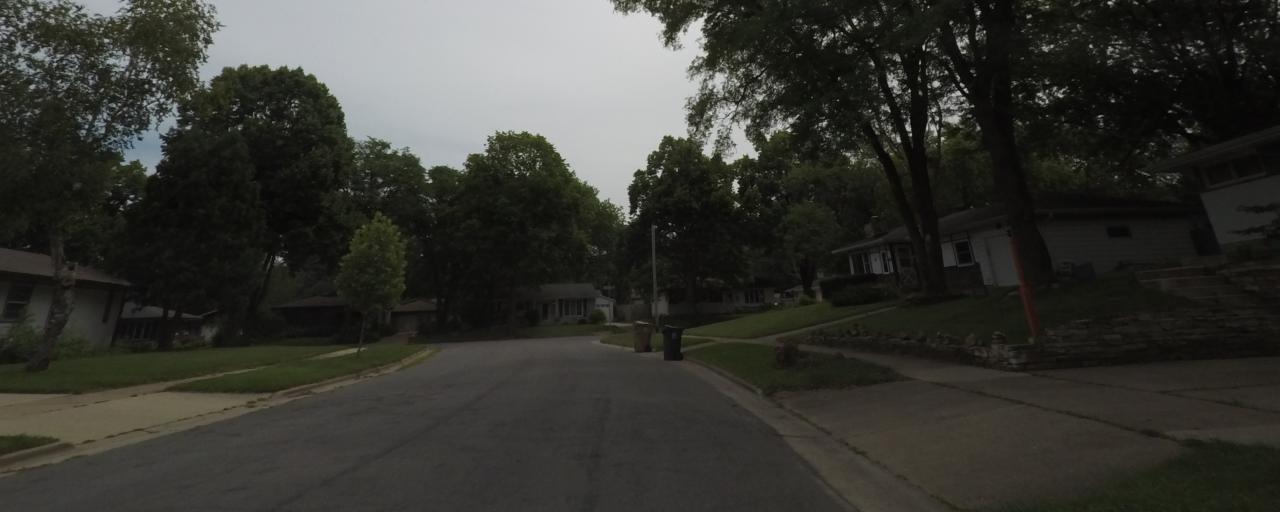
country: US
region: Wisconsin
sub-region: Dane County
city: Monona
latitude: 43.0805
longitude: -89.2990
